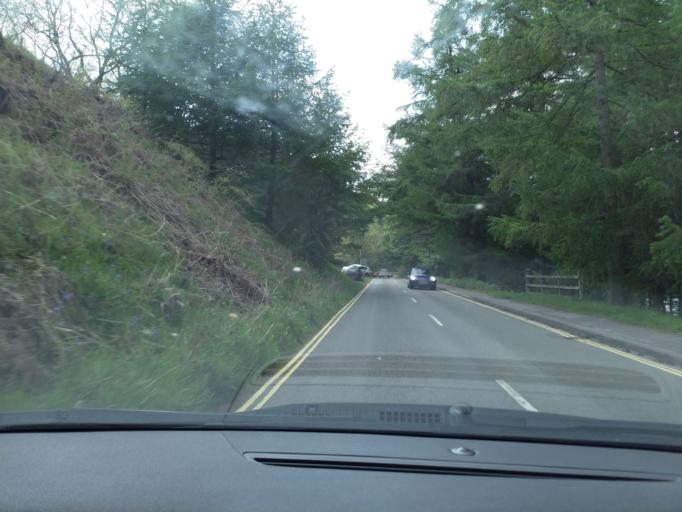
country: GB
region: England
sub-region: Derbyshire
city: Hope Valley
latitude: 53.3934
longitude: -1.7324
